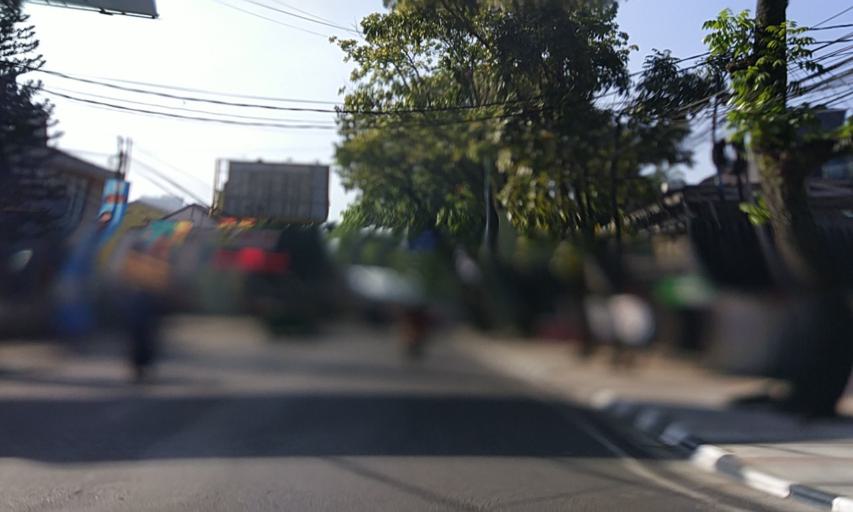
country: ID
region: West Java
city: Bandung
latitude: -6.8831
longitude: 107.6025
